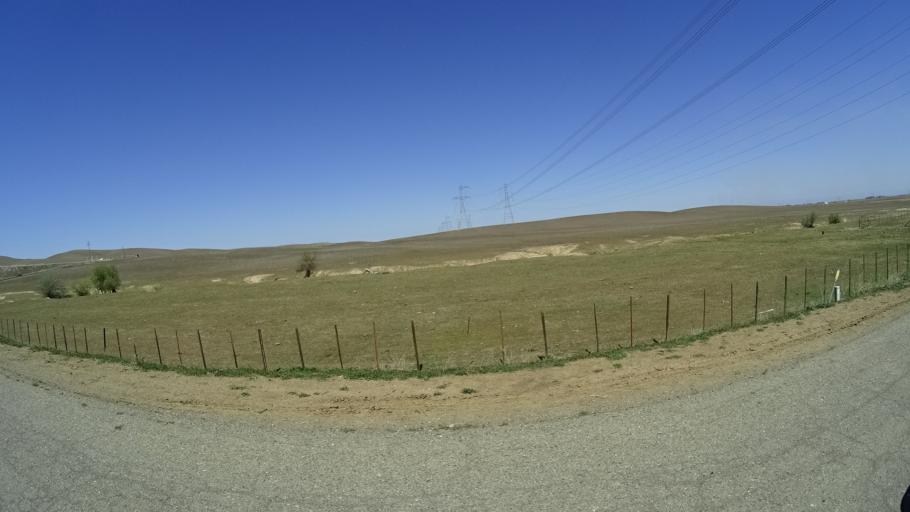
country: US
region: California
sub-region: Glenn County
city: Willows
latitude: 39.3997
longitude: -122.2854
